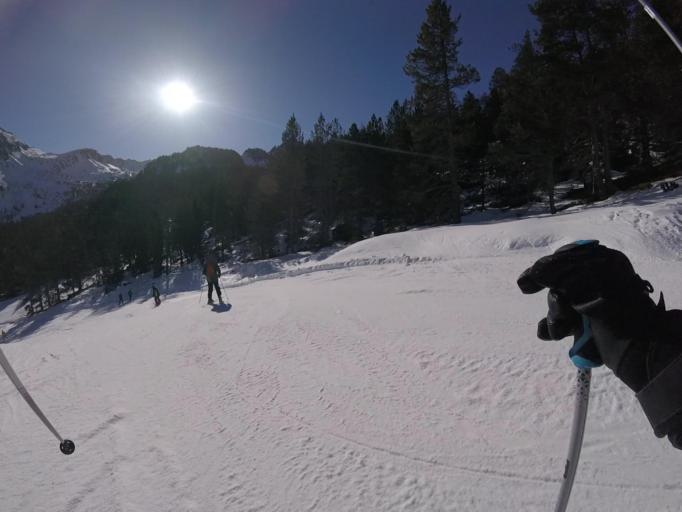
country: AD
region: Encamp
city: Pas de la Casa
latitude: 42.5288
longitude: 1.6920
